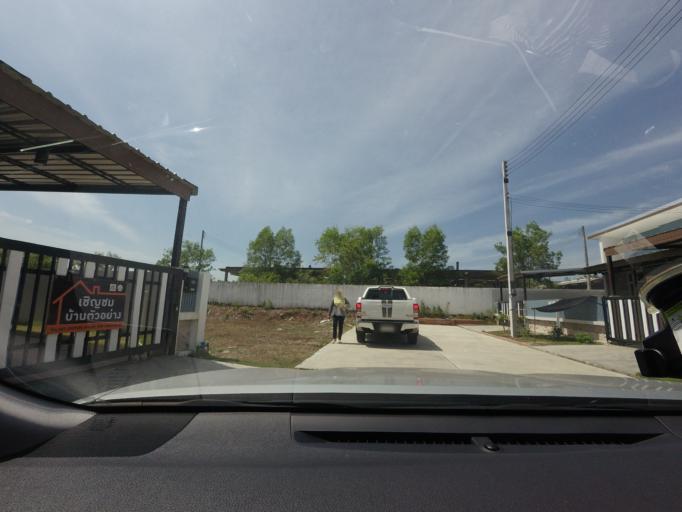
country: TH
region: Narathiwat
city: Narathiwat
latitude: 6.4497
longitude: 101.7920
